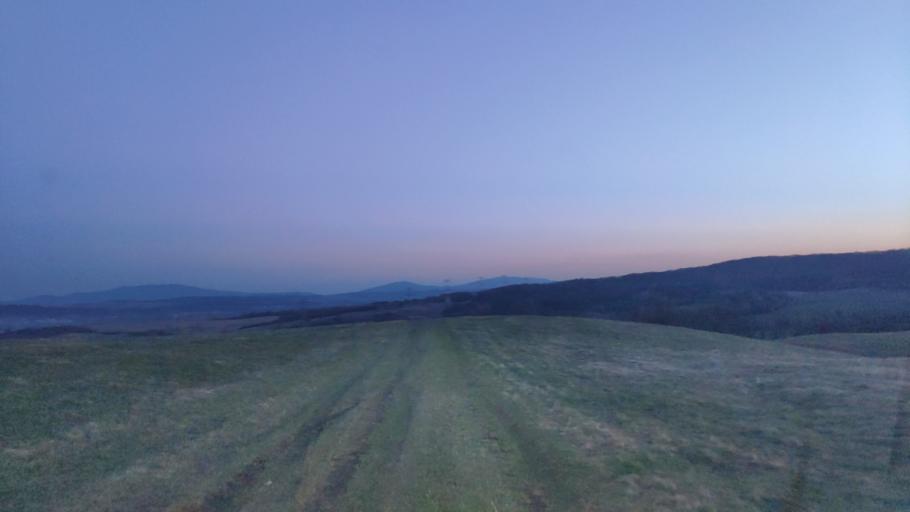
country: SK
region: Kosicky
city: Kosice
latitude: 48.8280
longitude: 21.2626
